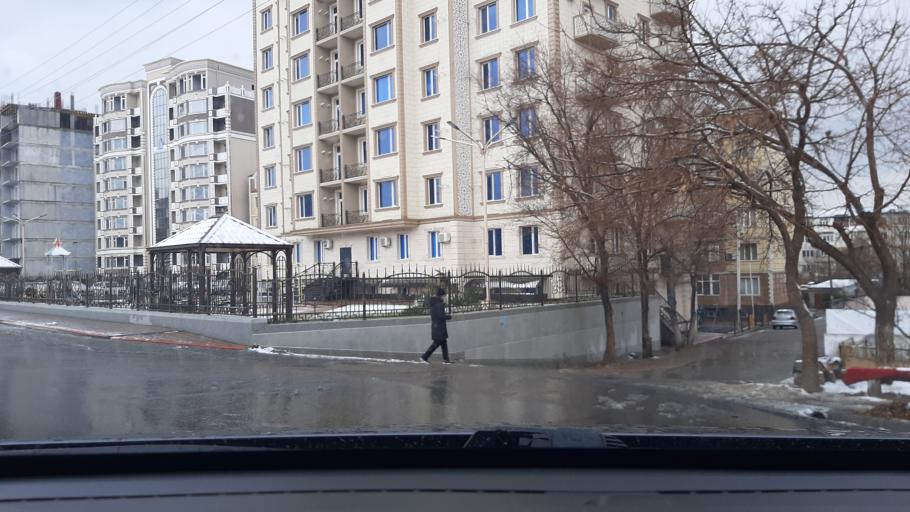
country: TJ
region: Viloyati Sughd
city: Khujand
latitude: 40.3011
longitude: 69.6077
